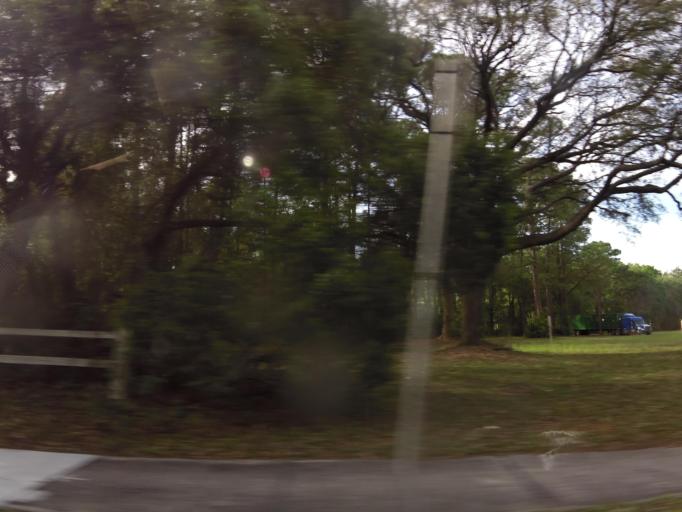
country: US
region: Florida
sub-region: Clay County
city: Bellair-Meadowbrook Terrace
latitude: 30.2661
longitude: -81.7767
